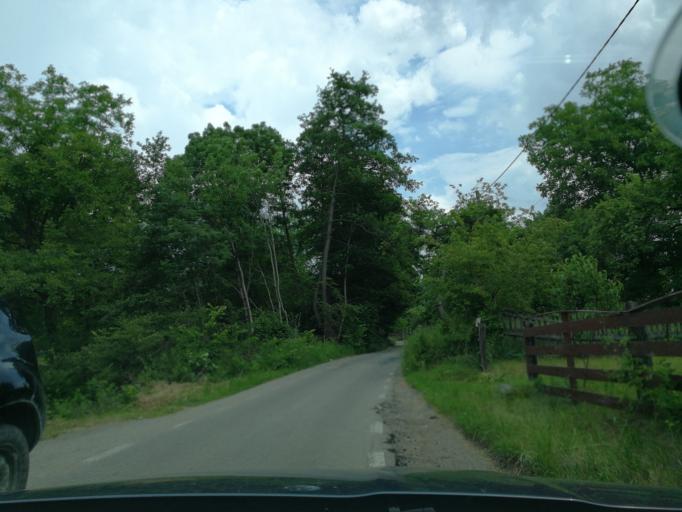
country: RO
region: Maramures
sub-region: Comuna Sisesti
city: Sisesti
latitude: 47.6174
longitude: 23.7237
